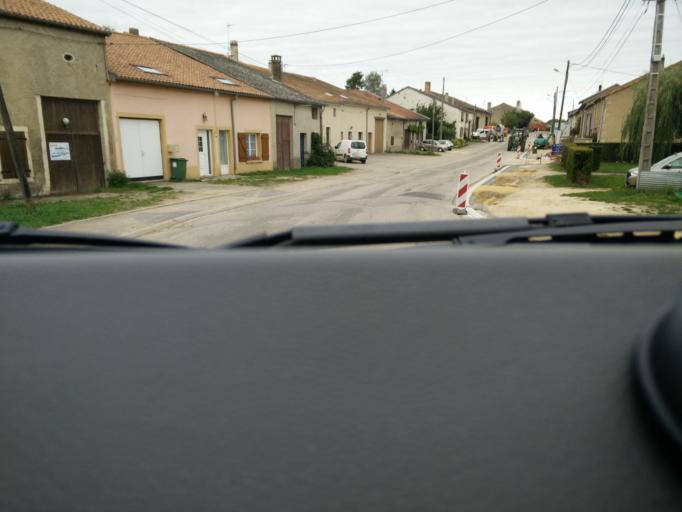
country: FR
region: Lorraine
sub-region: Departement de la Meuse
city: Vigneulles-les-Hattonchatel
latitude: 48.9623
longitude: 5.8262
